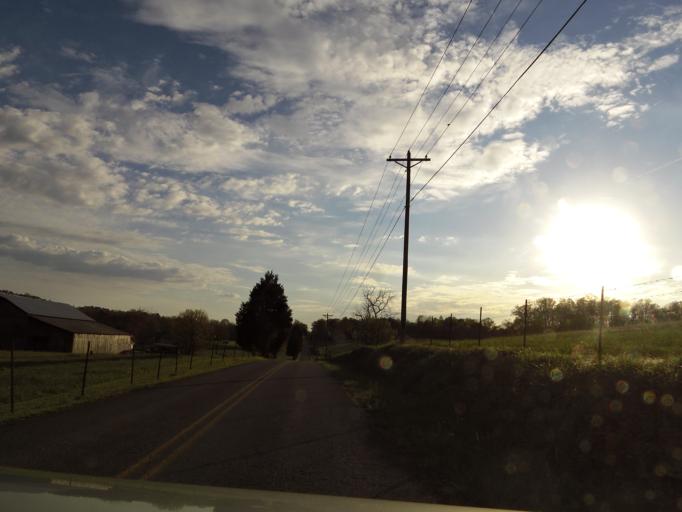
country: US
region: Tennessee
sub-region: Loudon County
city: Greenback
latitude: 35.6389
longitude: -84.0443
